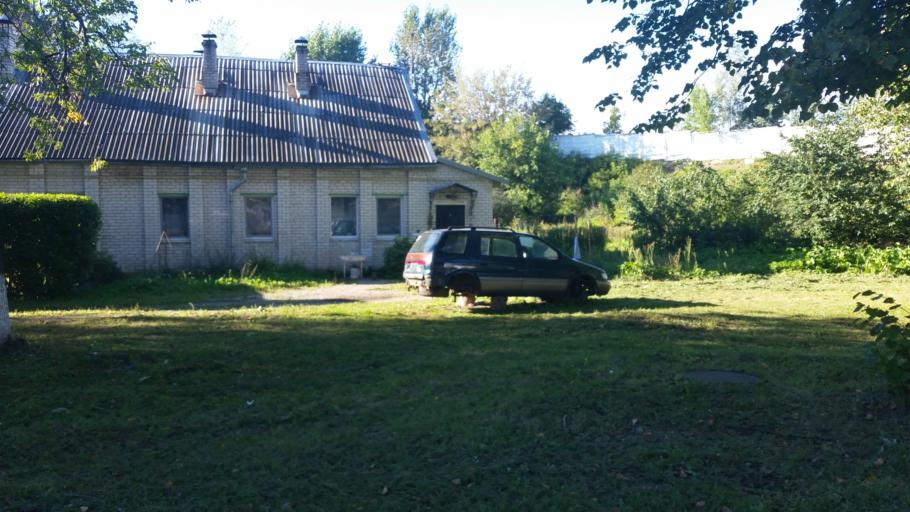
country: BY
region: Vitebsk
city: Vitebsk
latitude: 55.1772
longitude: 30.1839
